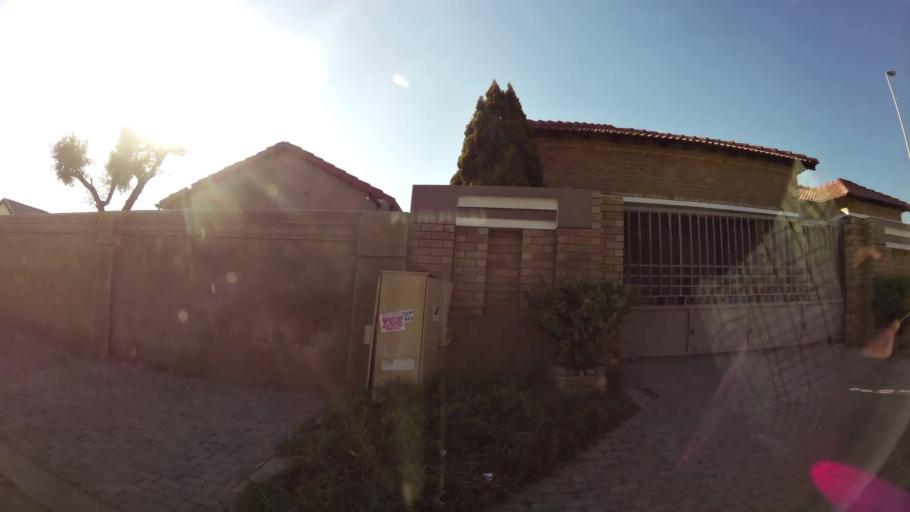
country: ZA
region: Gauteng
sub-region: City of Johannesburg Metropolitan Municipality
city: Modderfontein
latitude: -26.0422
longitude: 28.1579
